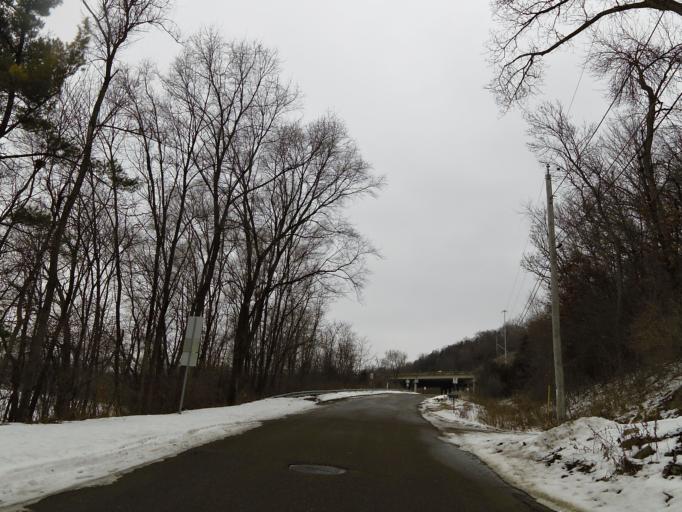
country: US
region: Wisconsin
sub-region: Saint Croix County
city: Hudson
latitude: 44.9610
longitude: -92.7502
